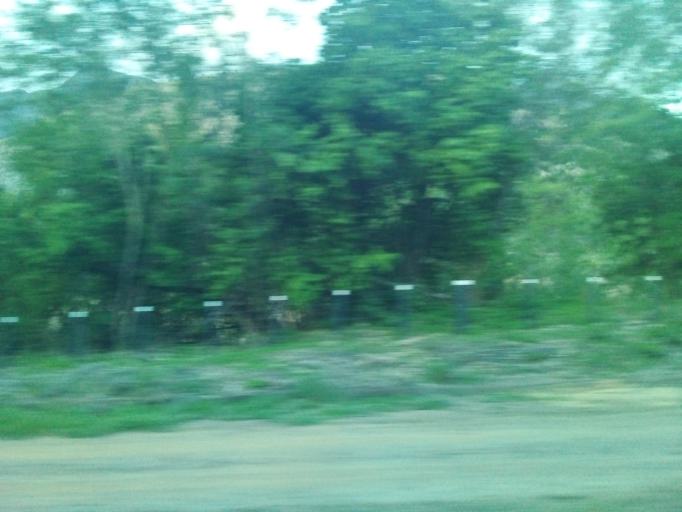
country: BR
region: Espirito Santo
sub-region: Baixo Guandu
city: Baixo Guandu
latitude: -19.5222
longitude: -40.8354
